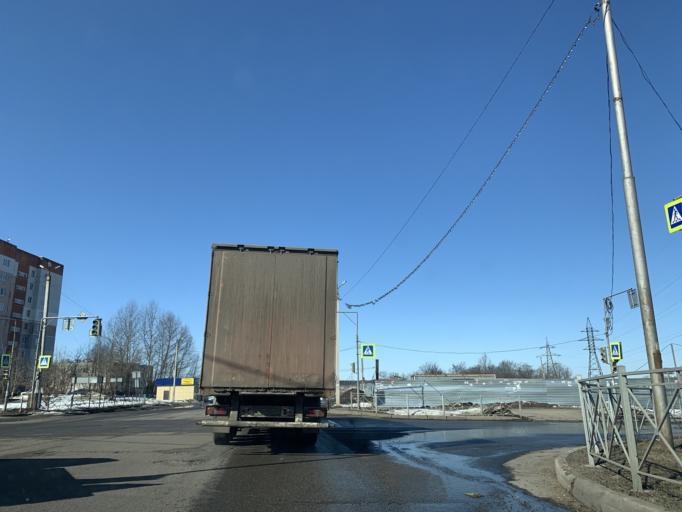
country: RU
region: Jaroslavl
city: Tutayev
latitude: 57.8655
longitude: 39.5083
